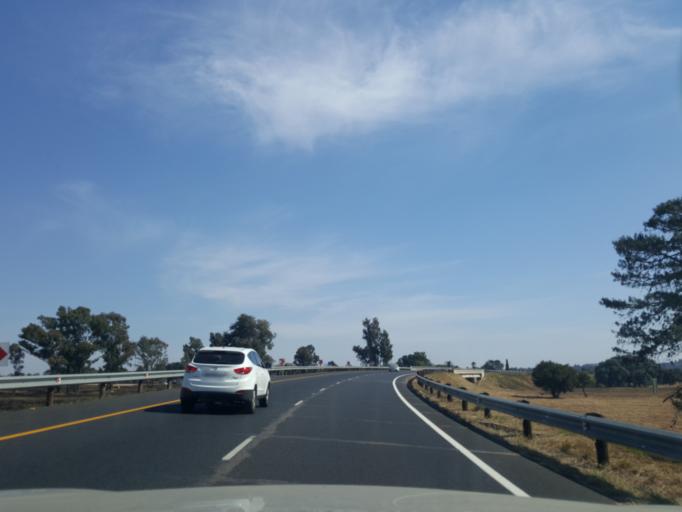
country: ZA
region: Mpumalanga
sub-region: Nkangala District Municipality
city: Witbank
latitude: -25.8962
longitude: 29.2570
